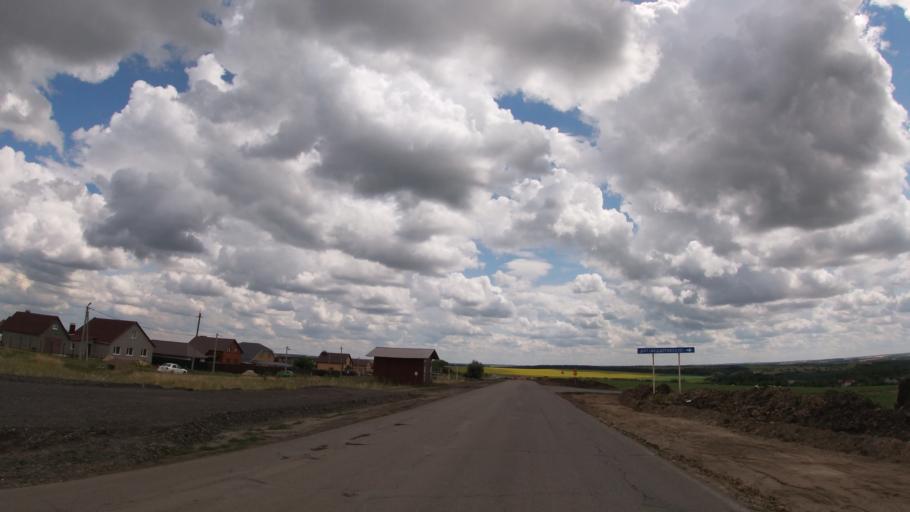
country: RU
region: Belgorod
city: Mayskiy
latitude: 50.5020
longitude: 36.4444
